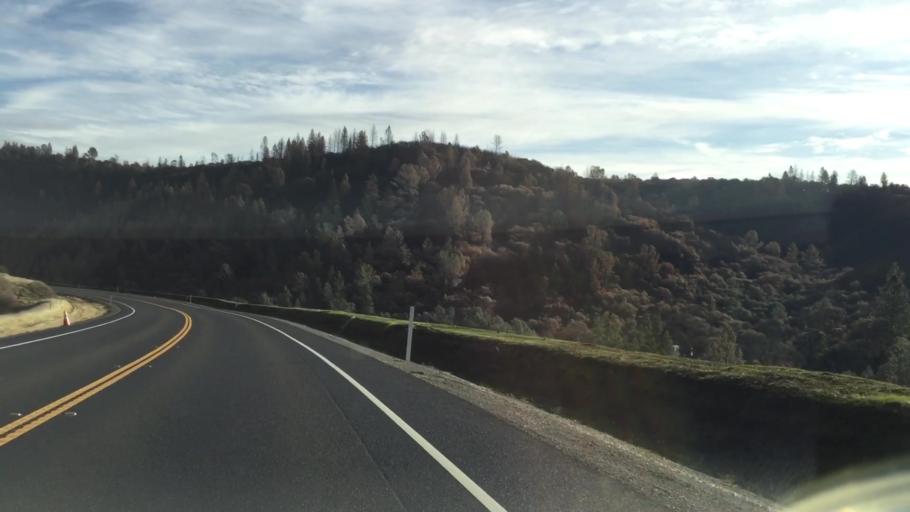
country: US
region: California
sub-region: Butte County
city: Paradise
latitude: 39.6542
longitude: -121.5428
